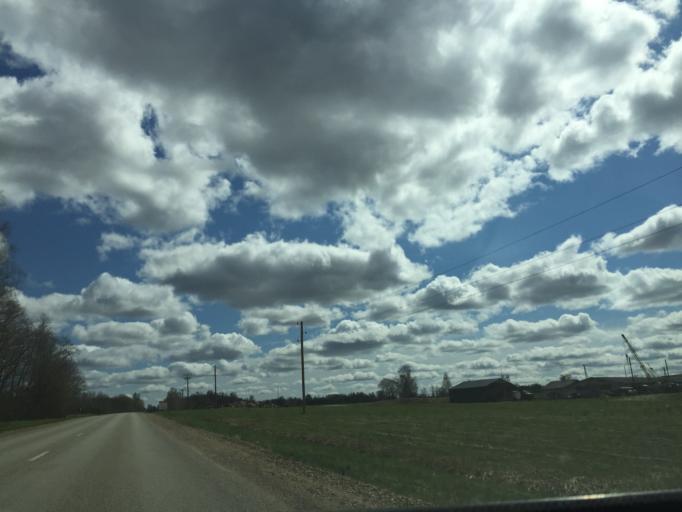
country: LV
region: Rezekne
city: Rezekne
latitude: 56.6629
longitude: 27.1784
